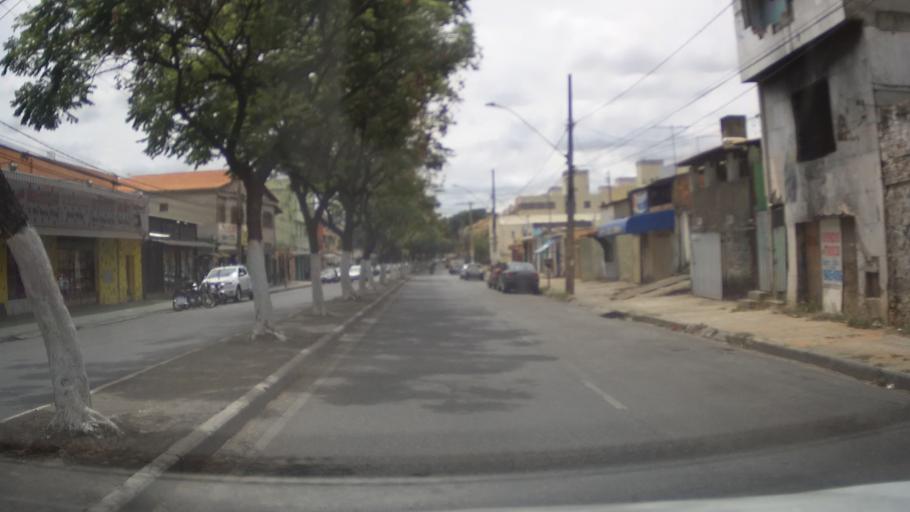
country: BR
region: Minas Gerais
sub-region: Ribeirao Das Neves
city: Ribeirao das Neves
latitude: -19.8039
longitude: -43.9776
